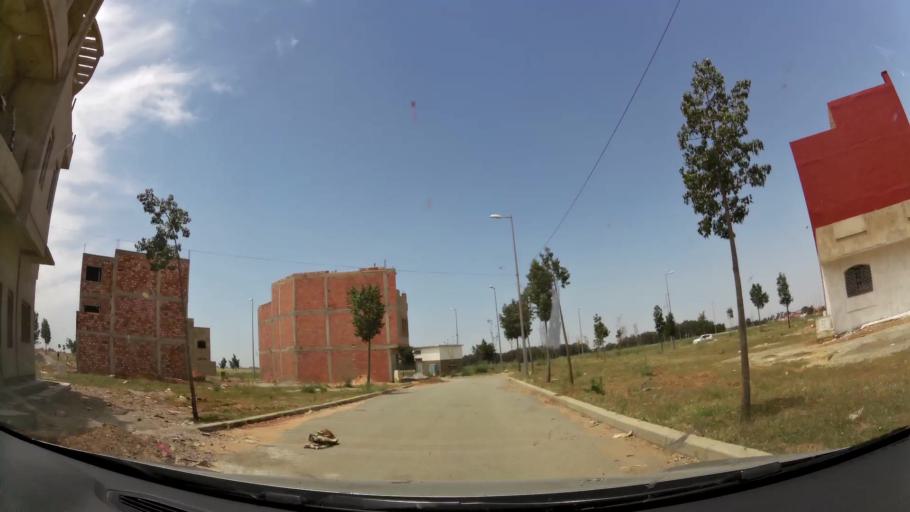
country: MA
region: Rabat-Sale-Zemmour-Zaer
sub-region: Khemisset
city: Khemisset
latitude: 33.8156
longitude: -6.0911
